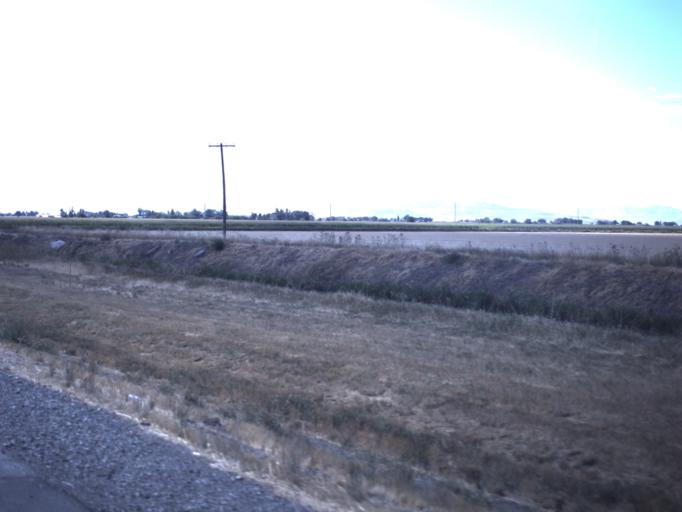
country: US
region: Utah
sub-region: Box Elder County
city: Elwood
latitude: 41.6970
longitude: -112.1418
